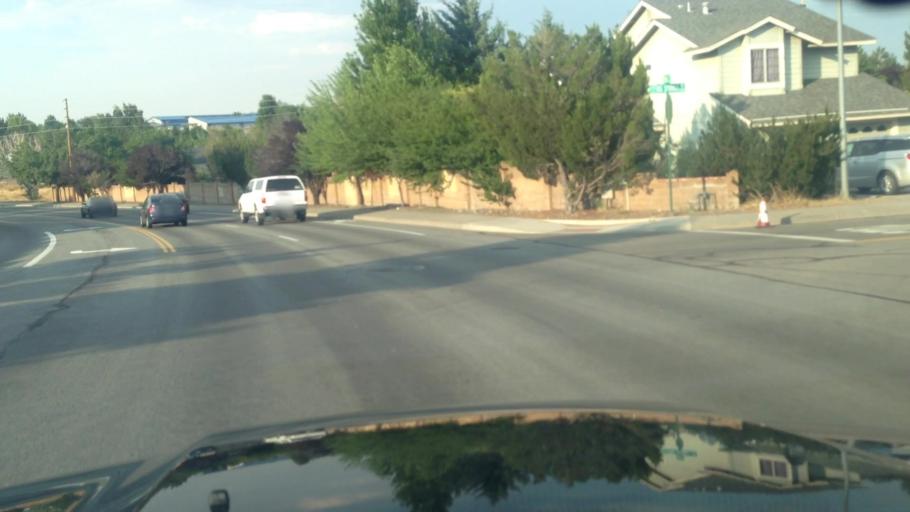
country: US
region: Nevada
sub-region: Washoe County
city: Mogul
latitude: 39.5205
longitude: -119.8830
